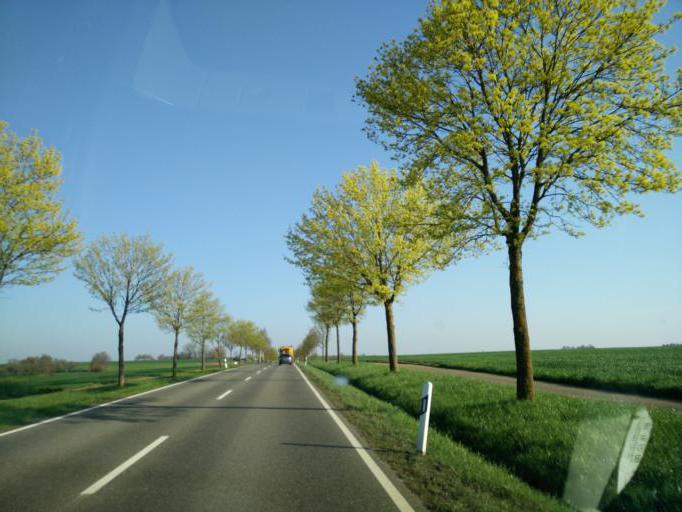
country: DE
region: Baden-Wuerttemberg
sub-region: Regierungsbezirk Stuttgart
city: Deckenpfronn
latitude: 48.6337
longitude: 8.8283
